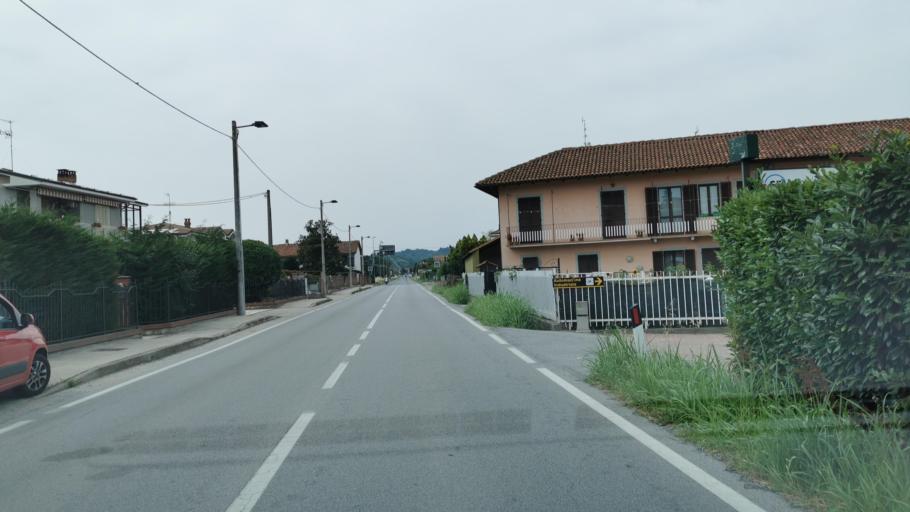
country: IT
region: Piedmont
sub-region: Provincia di Cuneo
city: Pocapaglia
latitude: 44.6899
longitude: 7.8933
